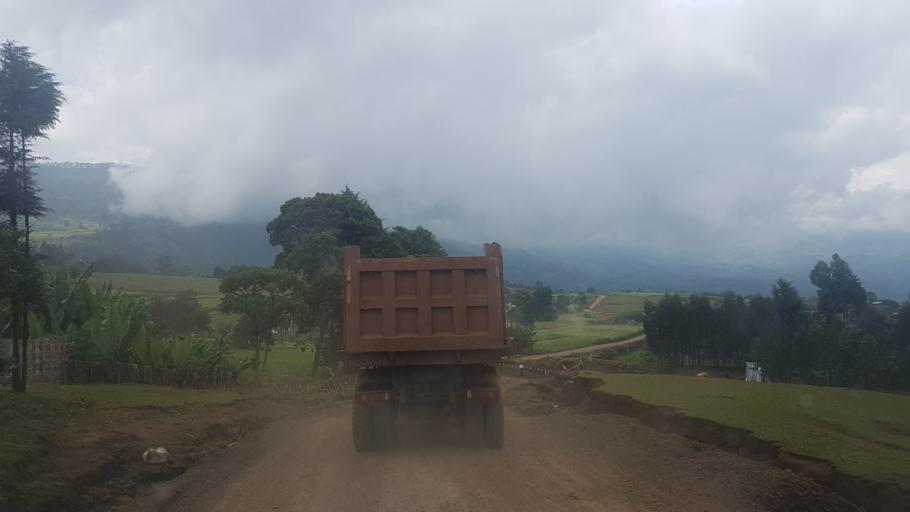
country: ET
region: Southern Nations, Nationalities, and People's Region
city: Arba Minch'
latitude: 6.3270
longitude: 37.5463
